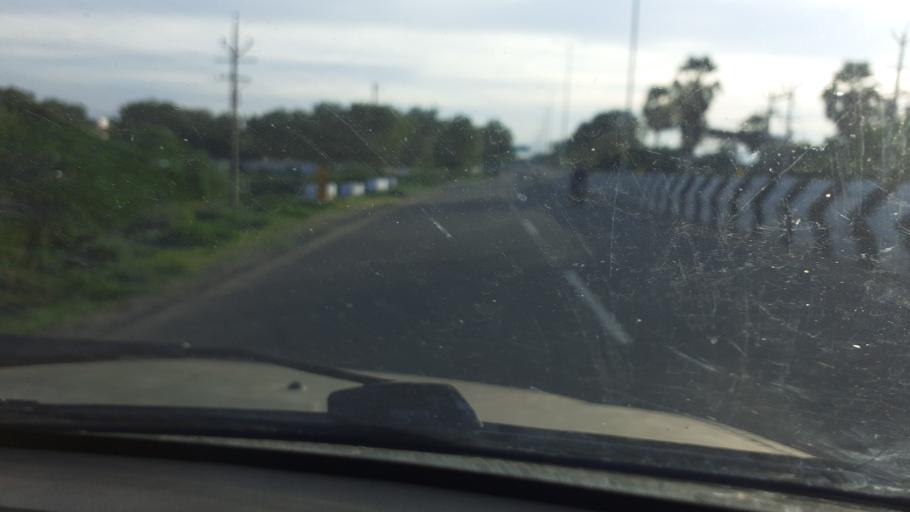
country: IN
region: Tamil Nadu
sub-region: Tirunelveli Kattabo
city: Tirunelveli
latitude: 8.6773
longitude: 77.7220
